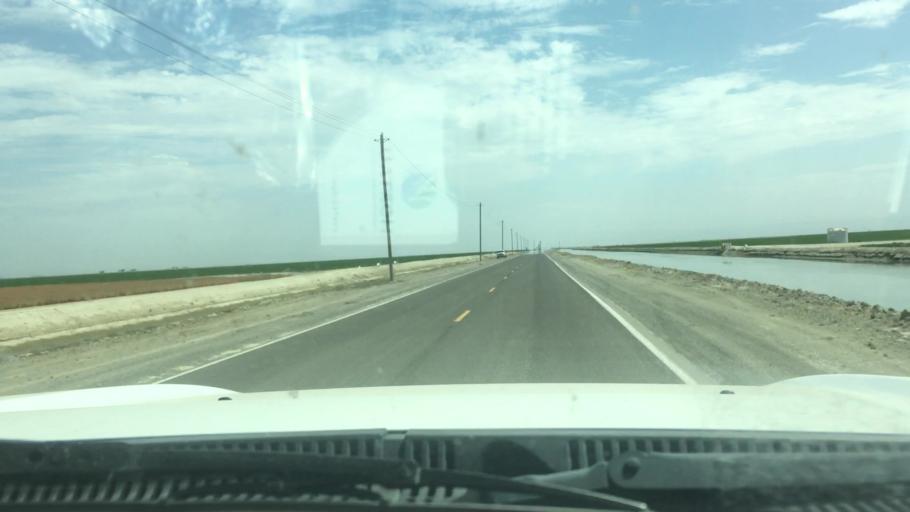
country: US
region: California
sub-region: Tulare County
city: Alpaugh
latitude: 35.8998
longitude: -119.5734
